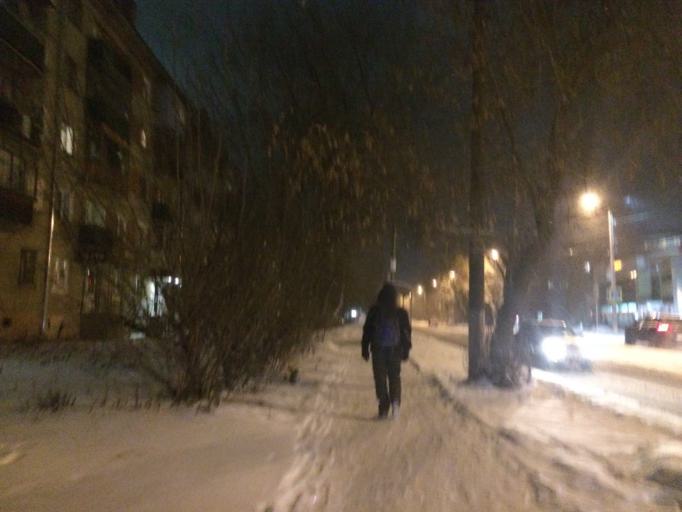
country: RU
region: Tula
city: Mendeleyevskiy
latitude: 54.1740
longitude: 37.5886
